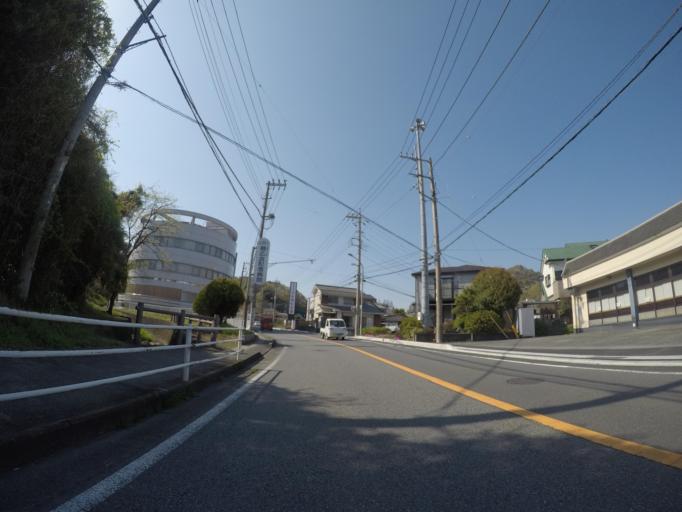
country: JP
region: Shizuoka
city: Mishima
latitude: 35.0387
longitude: 138.9257
